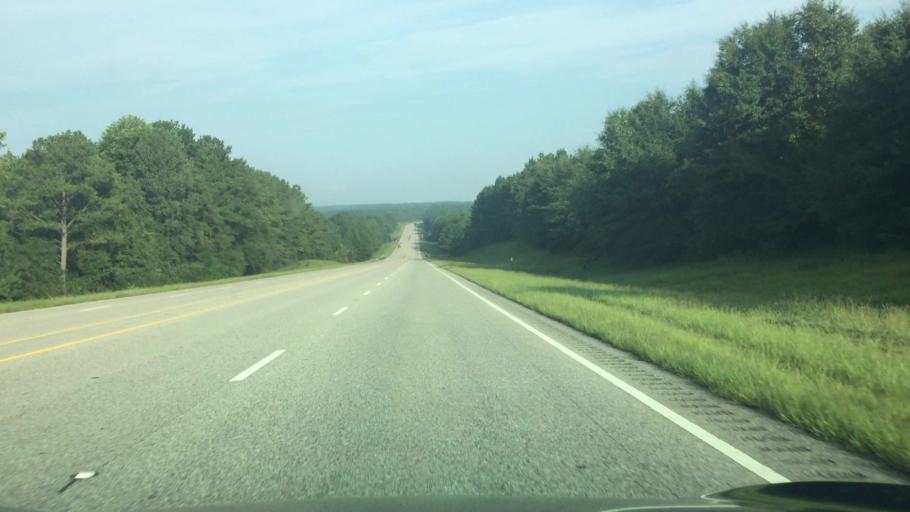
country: US
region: Alabama
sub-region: Butler County
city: Georgiana
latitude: 31.4628
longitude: -86.6482
